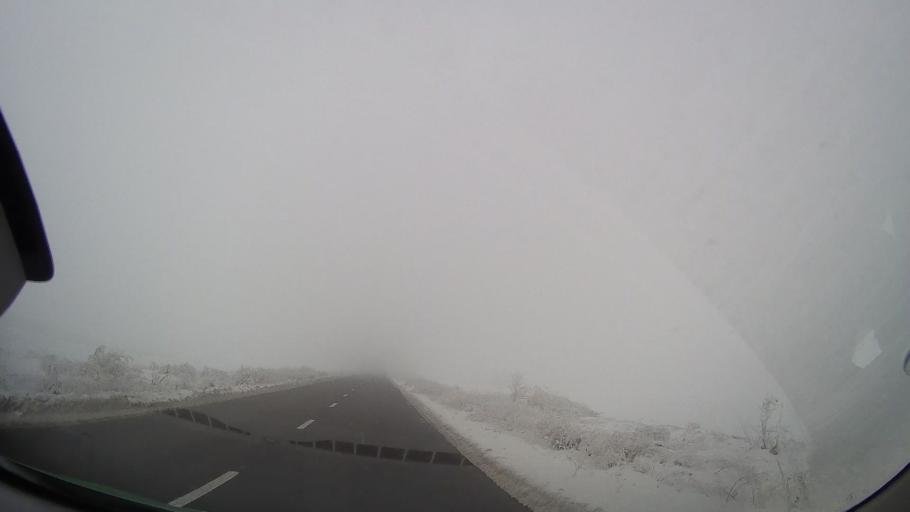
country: RO
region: Neamt
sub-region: Comuna Sabaoani
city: Sabaoani
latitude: 47.0398
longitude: 26.8521
